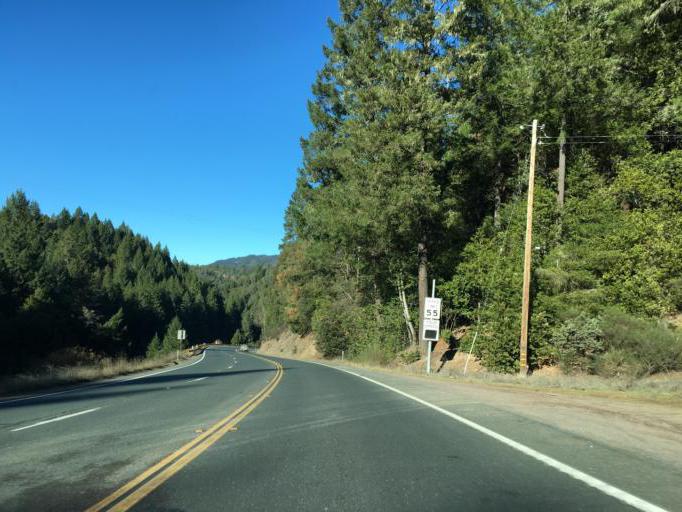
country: US
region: California
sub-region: Mendocino County
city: Brooktrails
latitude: 39.4747
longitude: -123.3635
